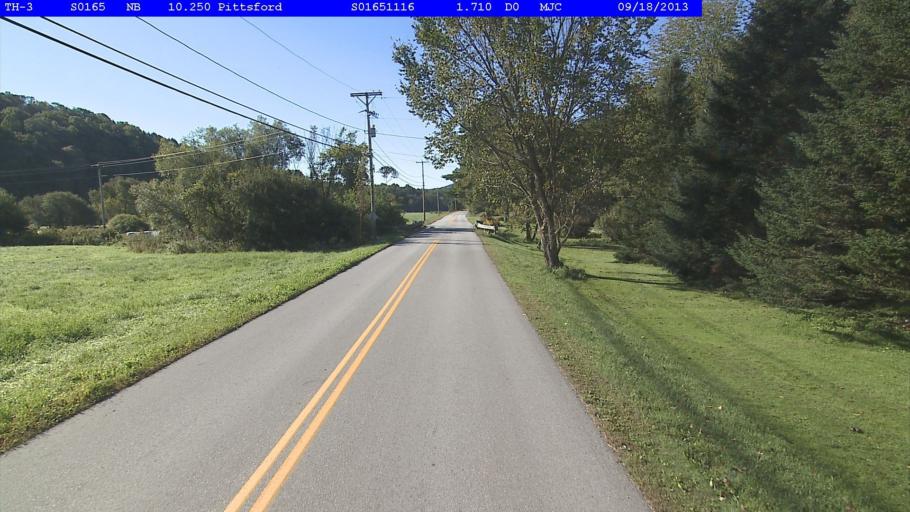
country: US
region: Vermont
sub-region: Rutland County
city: Rutland
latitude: 43.7179
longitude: -73.0062
